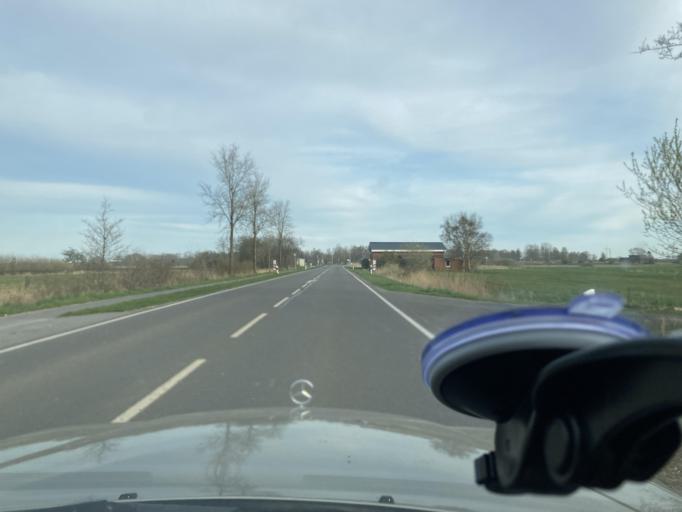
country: DE
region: Schleswig-Holstein
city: Stelle-Wittenwurth
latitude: 54.2601
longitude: 9.0556
